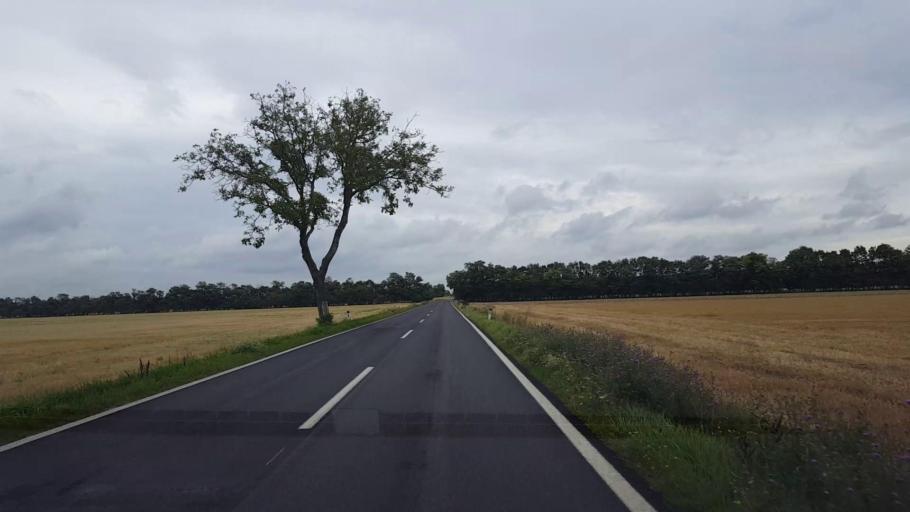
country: AT
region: Lower Austria
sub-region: Politischer Bezirk Wien-Umgebung
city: Zwolfaxing
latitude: 48.0839
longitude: 16.4768
